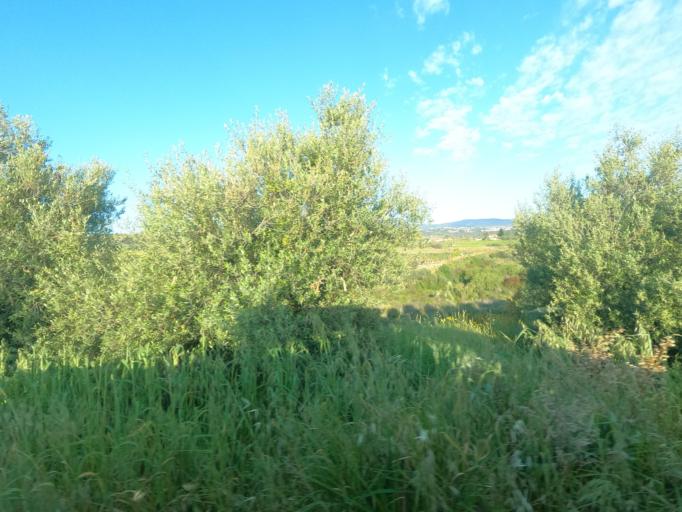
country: CY
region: Pafos
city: Polis
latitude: 35.0236
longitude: 32.4004
